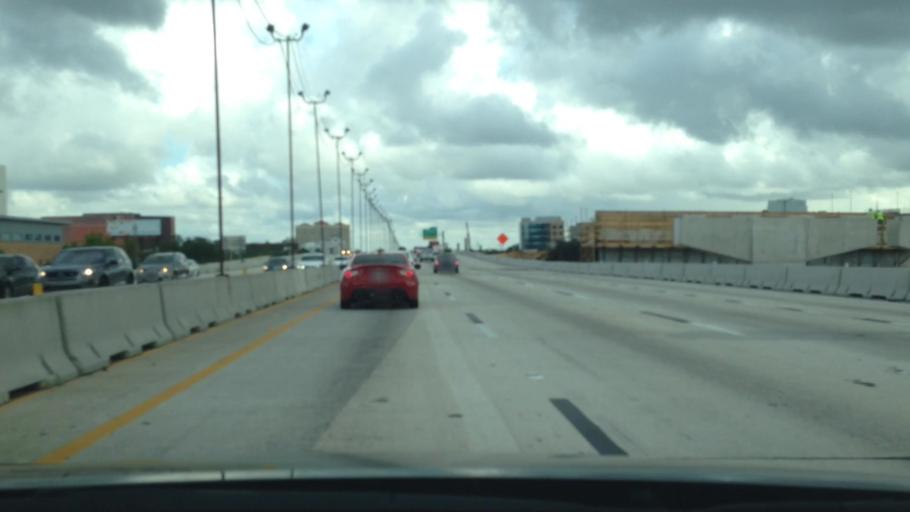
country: US
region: Florida
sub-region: Orange County
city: Orlando
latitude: 28.5436
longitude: -81.3818
